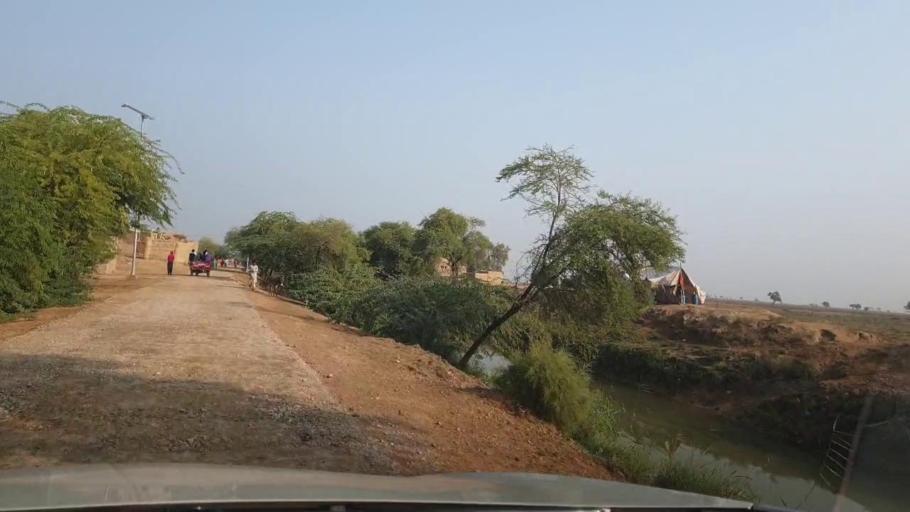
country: PK
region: Sindh
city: Sehwan
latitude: 26.3489
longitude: 67.7232
